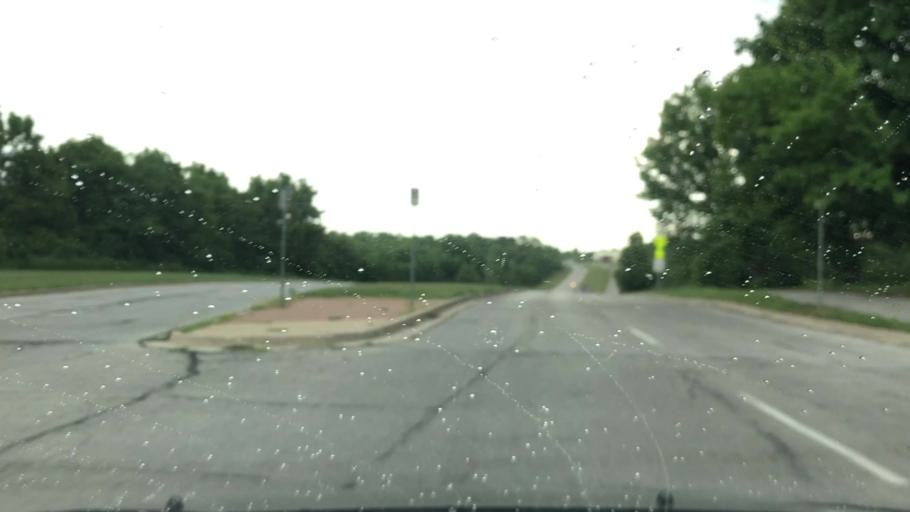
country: US
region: Missouri
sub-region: Jackson County
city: Grandview
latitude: 38.9295
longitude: -94.4857
